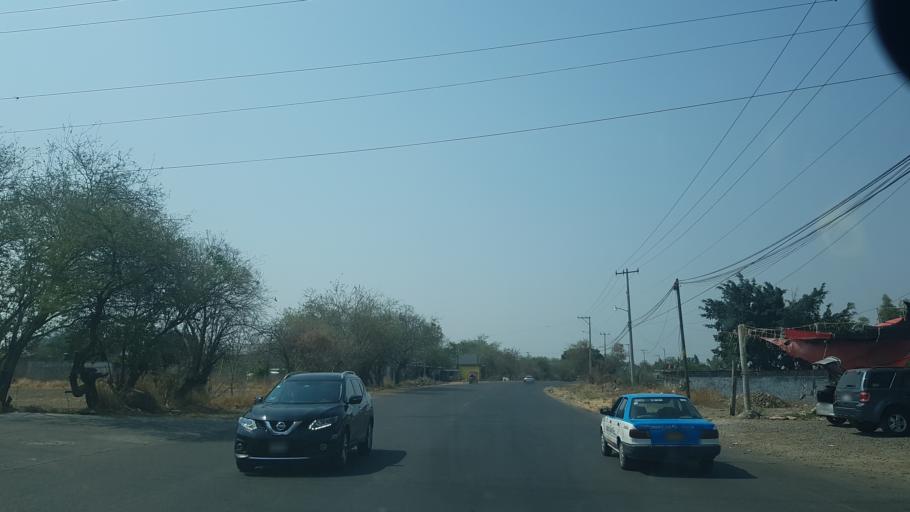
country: MX
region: Morelos
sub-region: Temoac
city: Huazulco
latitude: 18.7572
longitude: -98.7797
